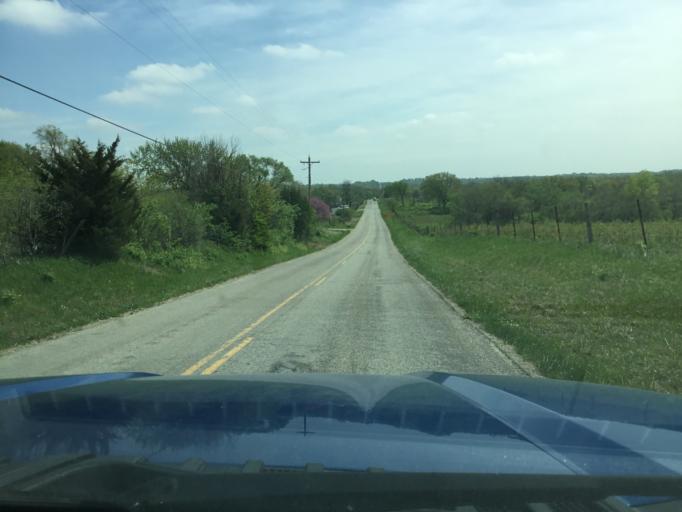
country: US
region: Kansas
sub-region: Shawnee County
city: Topeka
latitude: 39.1170
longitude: -95.5827
